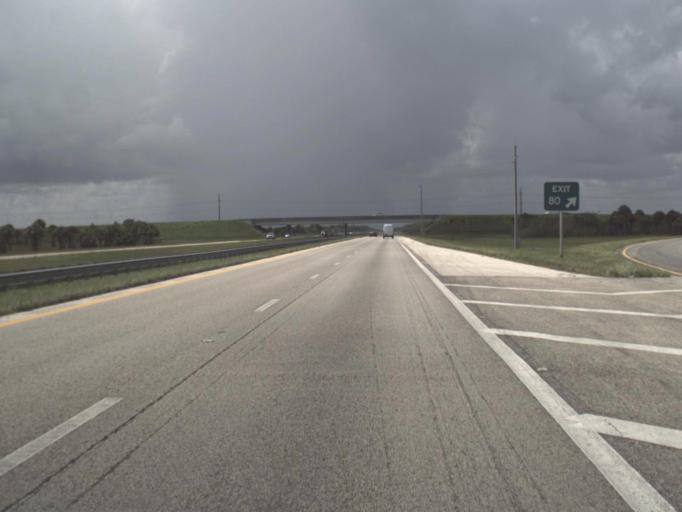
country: US
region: Florida
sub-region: Collier County
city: Immokalee
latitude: 26.1549
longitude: -81.3408
